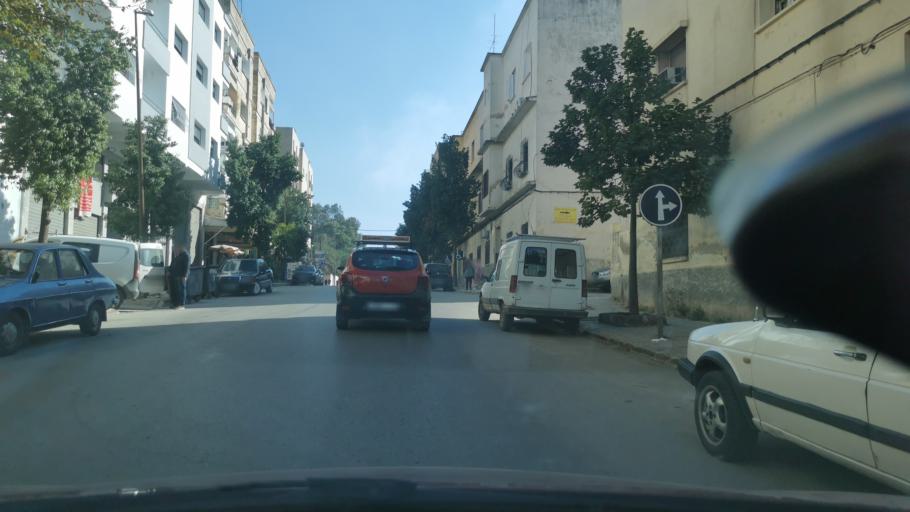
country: MA
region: Fes-Boulemane
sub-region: Fes
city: Fes
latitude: 34.0336
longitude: -4.9901
